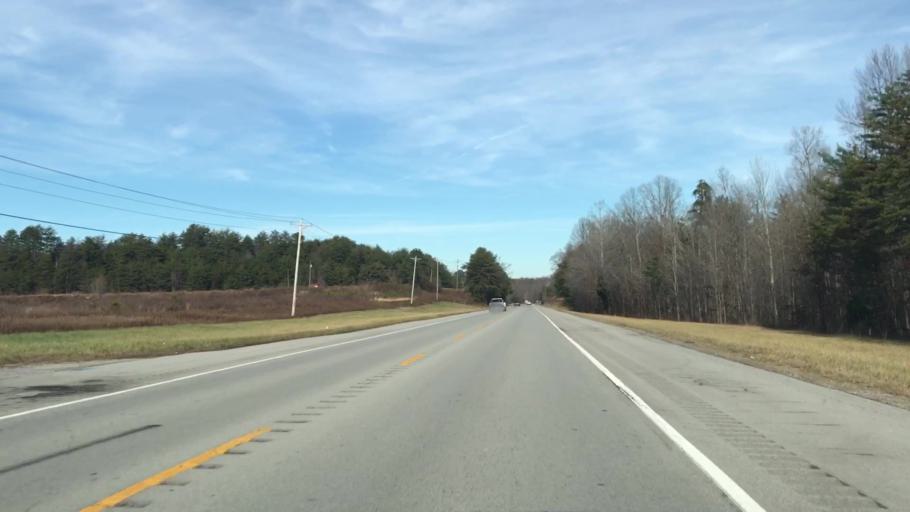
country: US
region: Kentucky
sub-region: McCreary County
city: Whitley City
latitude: 36.8829
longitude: -84.4950
